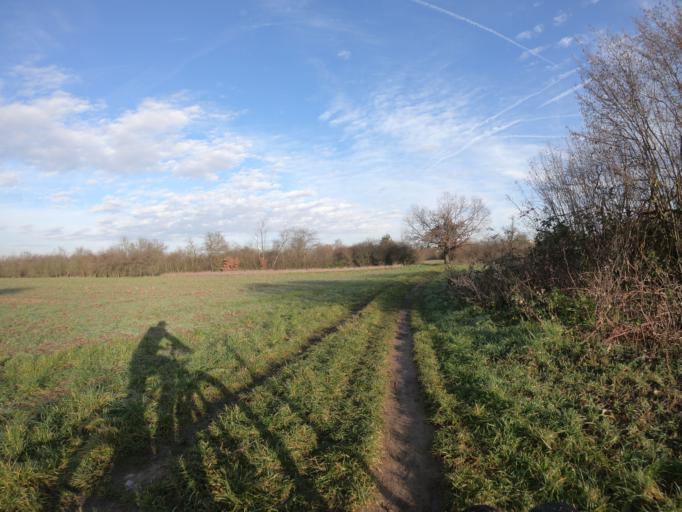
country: DE
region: Hesse
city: Morfelden-Walldorf
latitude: 49.9959
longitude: 8.5806
